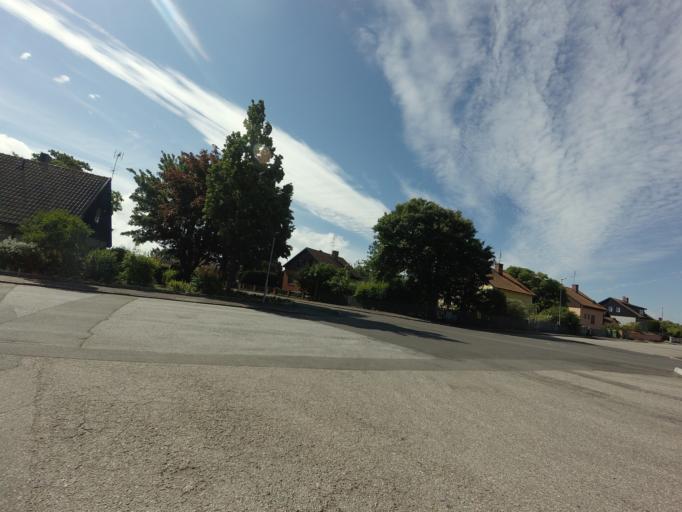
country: SE
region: Skane
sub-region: Simrishamns Kommun
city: Simrishamn
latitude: 55.4732
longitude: 14.2789
